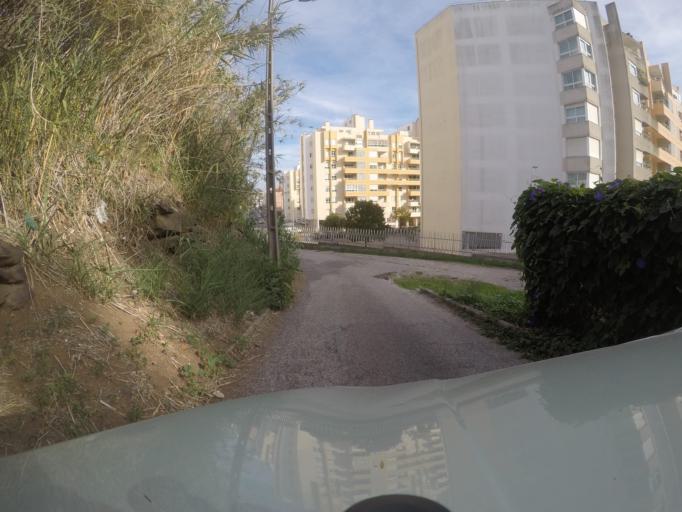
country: PT
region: Lisbon
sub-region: Amadora
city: Amadora
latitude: 38.7564
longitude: -9.2240
